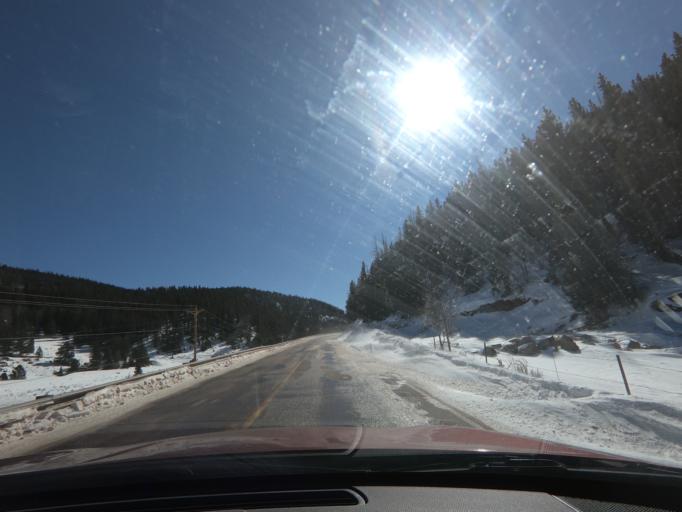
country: US
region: Colorado
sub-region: Teller County
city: Cripple Creek
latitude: 38.7545
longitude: -105.1041
